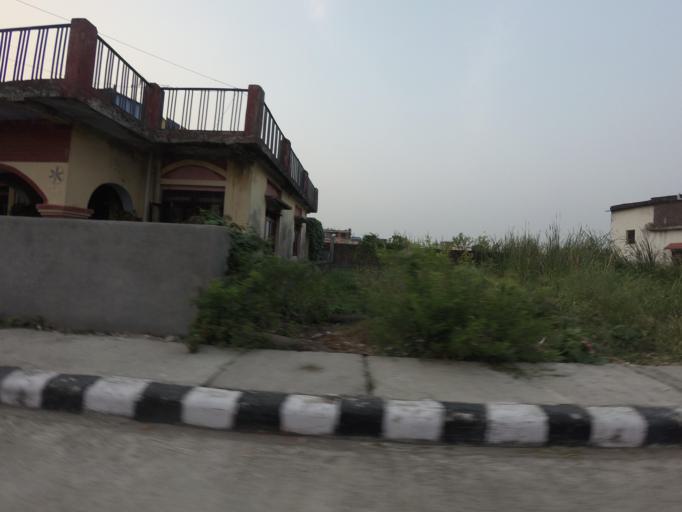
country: NP
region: Western Region
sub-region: Lumbini Zone
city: Bhairahawa
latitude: 27.5044
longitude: 83.4595
